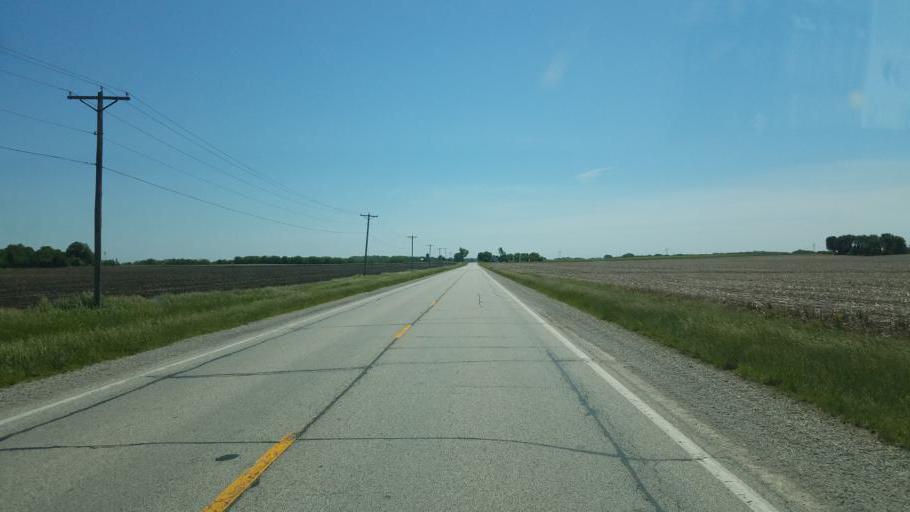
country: US
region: Illinois
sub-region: McLean County
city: Heyworth
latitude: 40.3121
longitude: -89.0447
